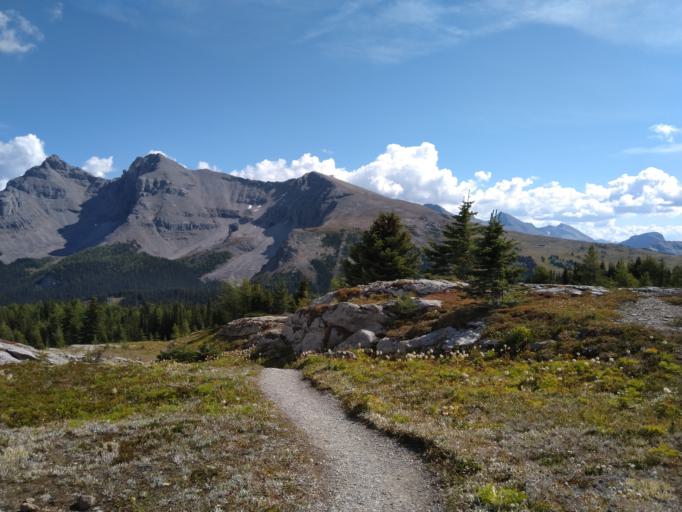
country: CA
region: Alberta
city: Banff
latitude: 51.0843
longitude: -115.7904
